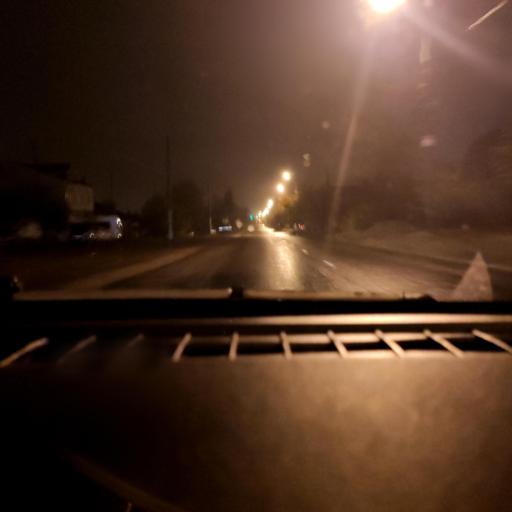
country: RU
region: Voronezj
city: Voronezh
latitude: 51.6976
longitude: 39.1771
